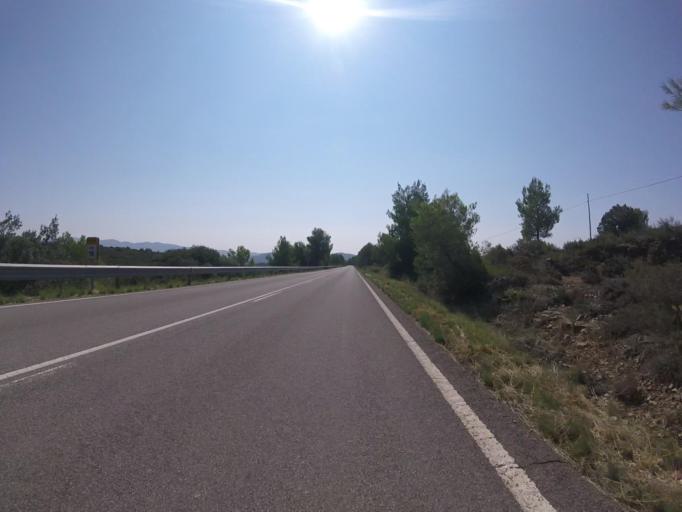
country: ES
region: Valencia
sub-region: Provincia de Castello
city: Benafigos
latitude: 40.2462
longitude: -0.1976
